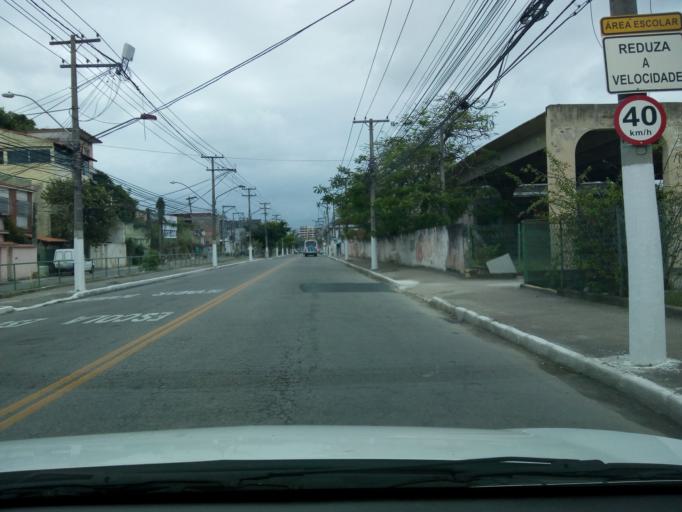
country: BR
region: Rio de Janeiro
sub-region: Niteroi
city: Niteroi
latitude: -22.8682
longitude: -43.1041
